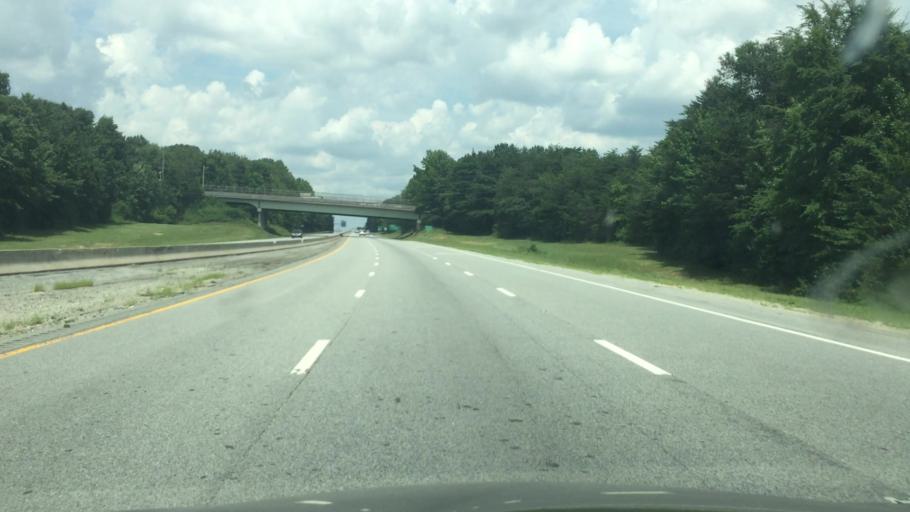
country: US
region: North Carolina
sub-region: Guilford County
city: Greensboro
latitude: 36.0068
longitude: -79.8264
